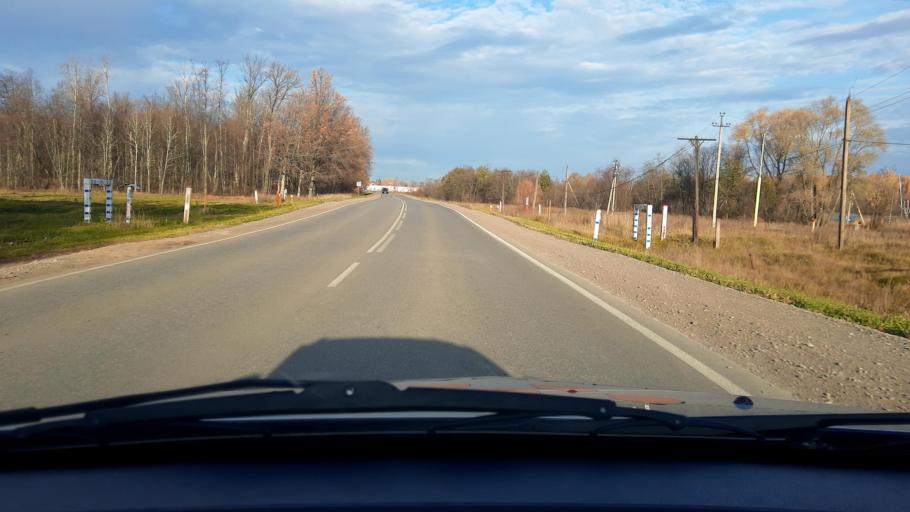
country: RU
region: Bashkortostan
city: Mikhaylovka
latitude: 54.8065
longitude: 55.8218
